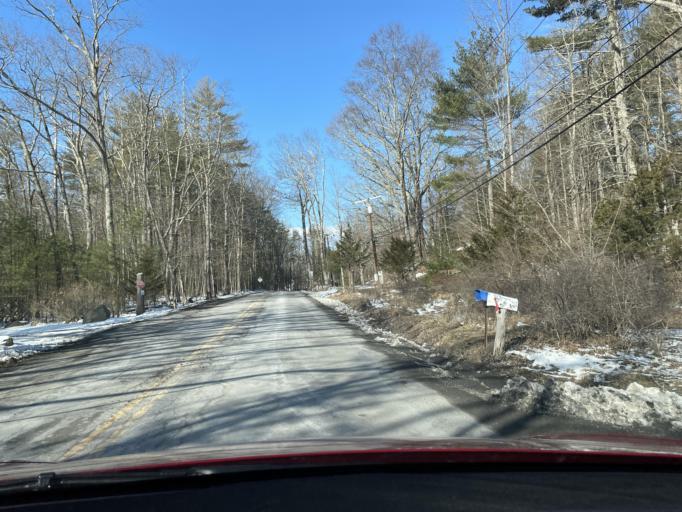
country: US
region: New York
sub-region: Ulster County
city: Woodstock
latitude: 42.0492
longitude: -74.1282
